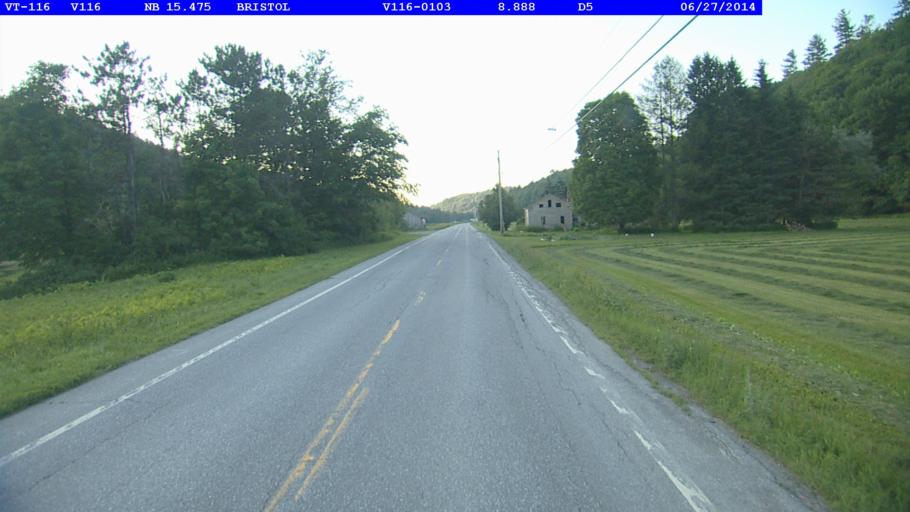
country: US
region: Vermont
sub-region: Addison County
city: Bristol
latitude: 44.1387
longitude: -73.0453
